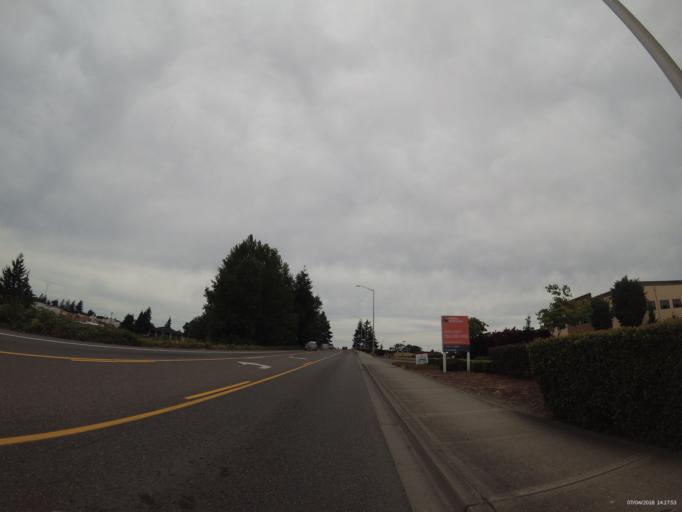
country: US
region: Washington
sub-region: Pierce County
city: McChord Air Force Base
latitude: 47.1573
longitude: -122.4835
